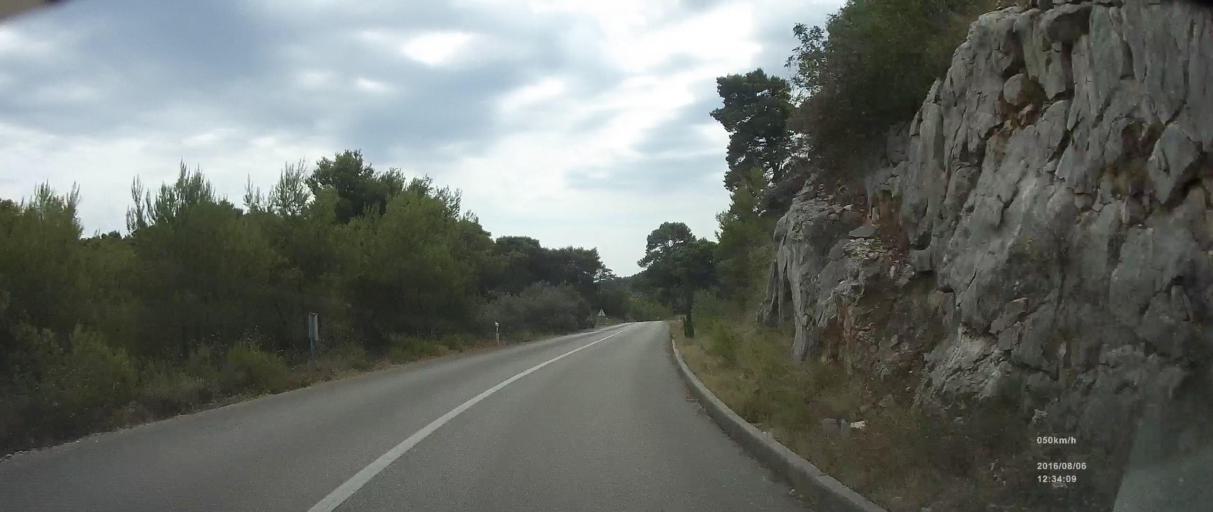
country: HR
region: Dubrovacko-Neretvanska
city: Ston
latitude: 42.7105
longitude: 17.7284
